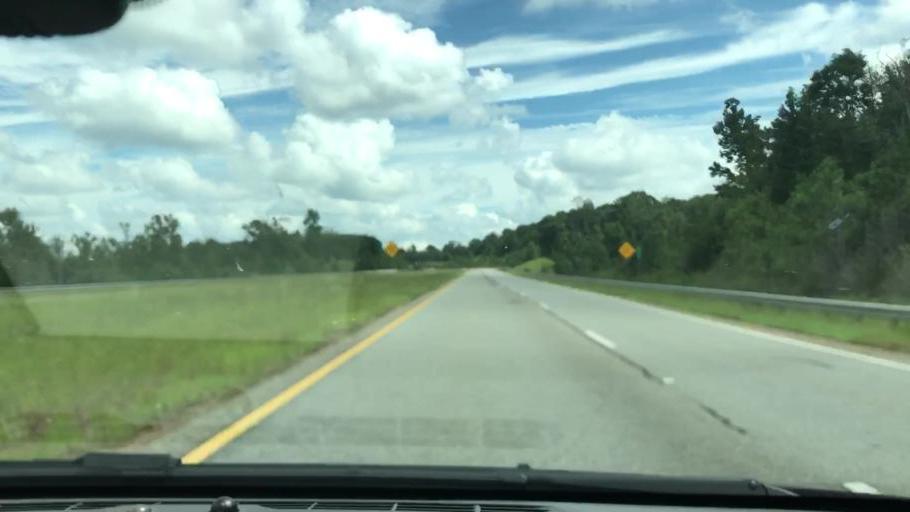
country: US
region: Georgia
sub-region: Stewart County
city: Lumpkin
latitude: 32.0579
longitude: -84.8022
